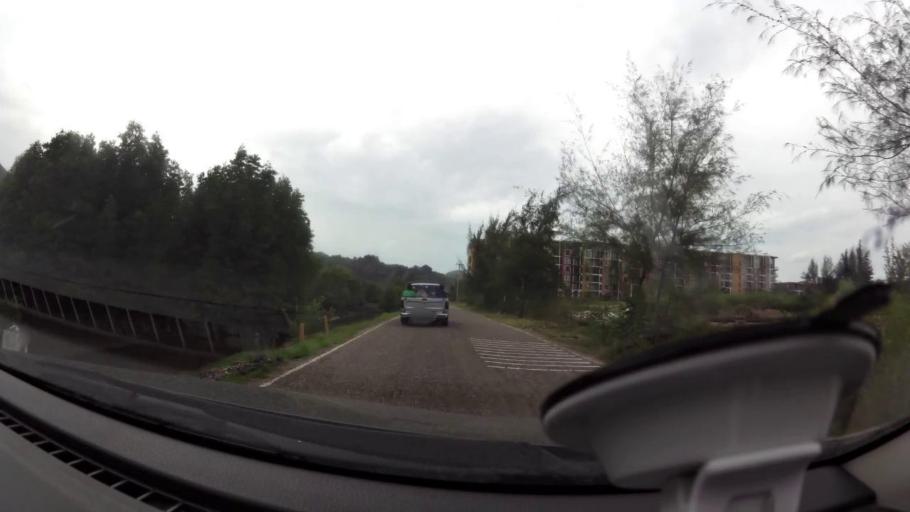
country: TH
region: Prachuap Khiri Khan
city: Pran Buri
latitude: 12.4186
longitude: 99.9806
